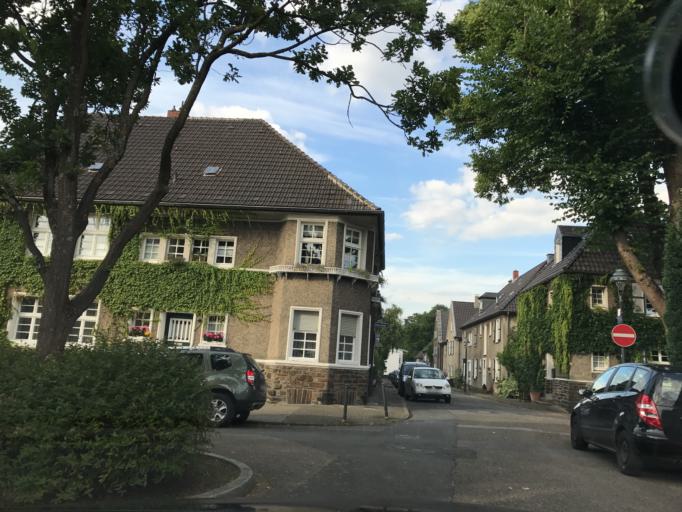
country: DE
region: North Rhine-Westphalia
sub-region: Regierungsbezirk Dusseldorf
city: Essen
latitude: 51.4321
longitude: 6.9791
